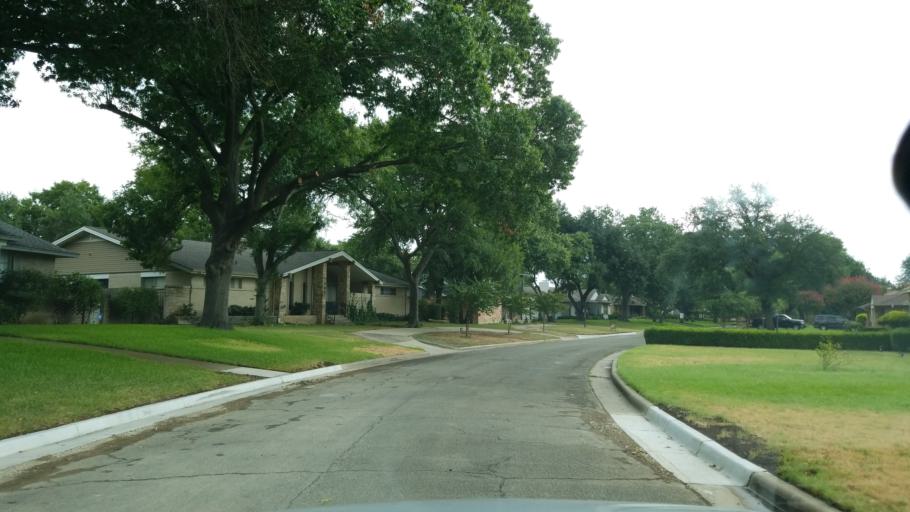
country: US
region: Texas
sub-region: Dallas County
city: Duncanville
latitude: 32.6702
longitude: -96.8468
